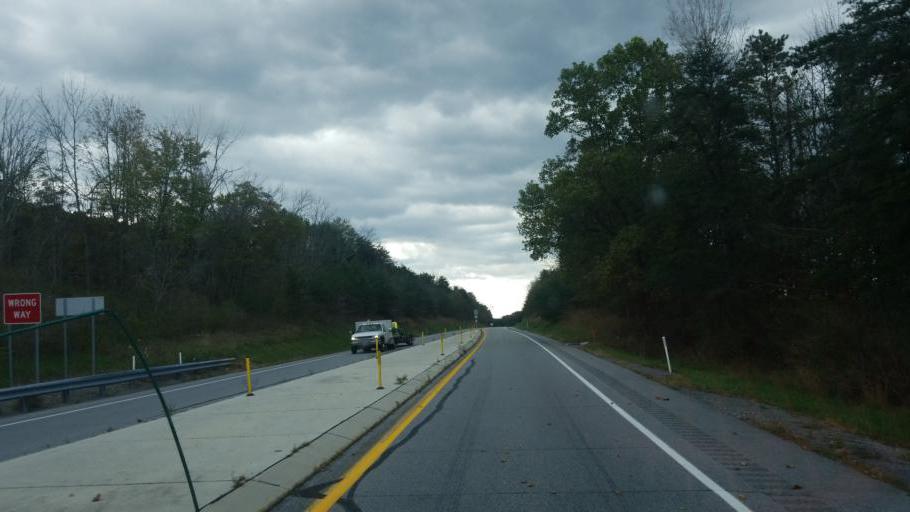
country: US
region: Pennsylvania
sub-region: Fulton County
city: McConnellsburg
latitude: 39.9458
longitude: -78.0211
